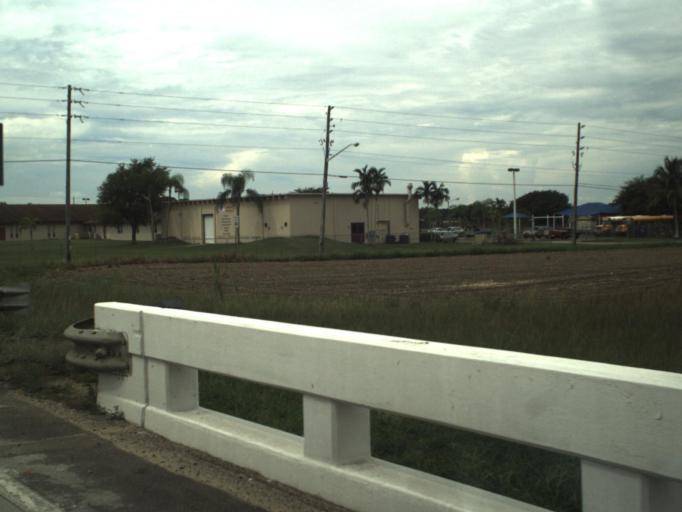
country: US
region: Florida
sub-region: Miami-Dade County
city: Homestead
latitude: 25.5069
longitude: -80.4778
